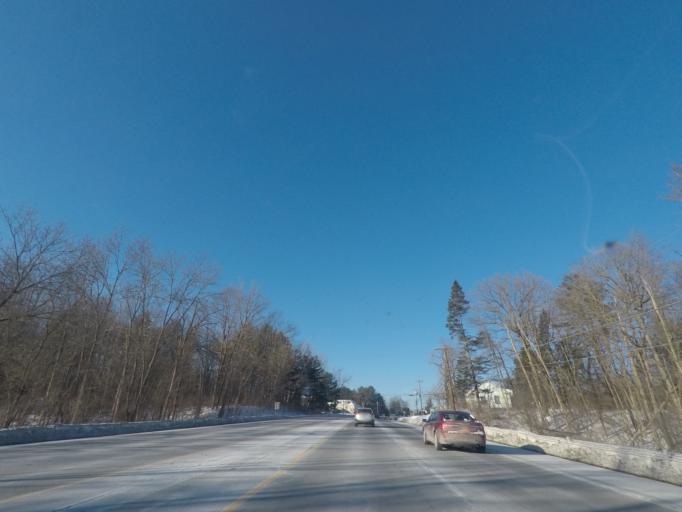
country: US
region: New York
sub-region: Saratoga County
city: Saratoga Springs
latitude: 43.0412
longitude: -73.7905
